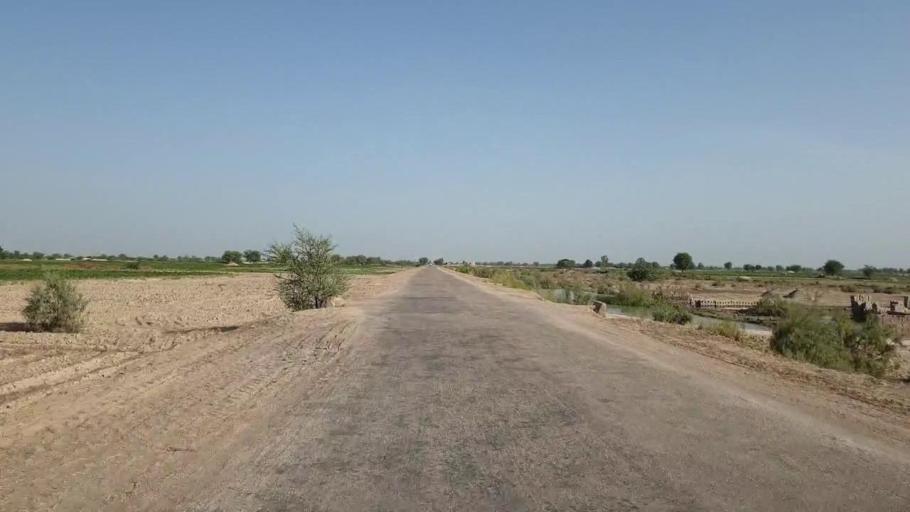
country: PK
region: Sindh
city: Nawabshah
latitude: 26.1476
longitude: 68.4492
